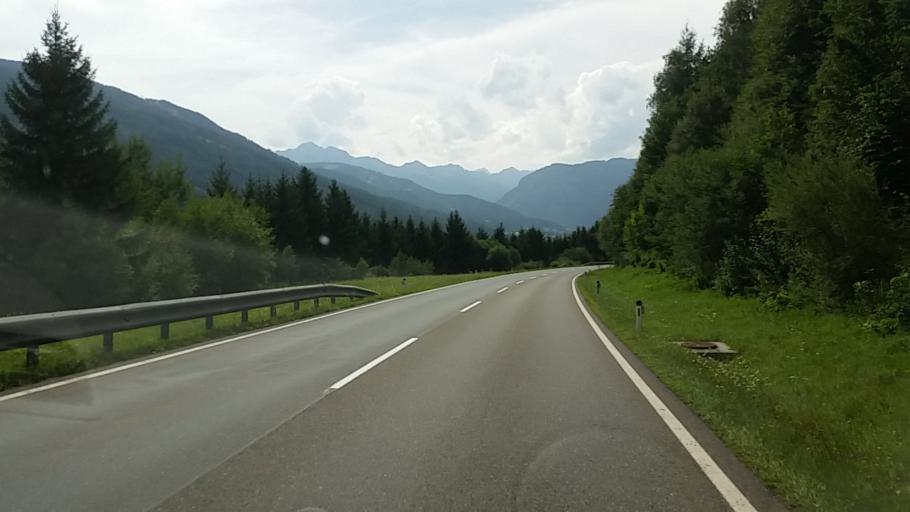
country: AT
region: Salzburg
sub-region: Politischer Bezirk Tamsweg
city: Sankt Margarethen im Lungau
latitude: 47.0915
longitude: 13.6883
